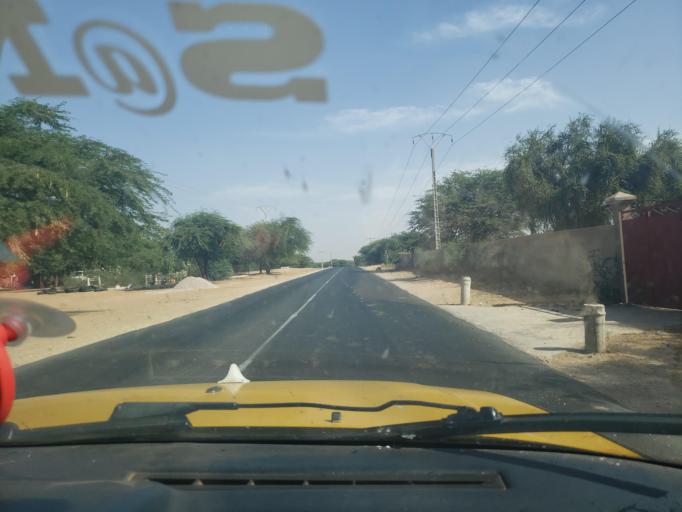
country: SN
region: Saint-Louis
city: Saint-Louis
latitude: 15.9277
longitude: -16.3223
